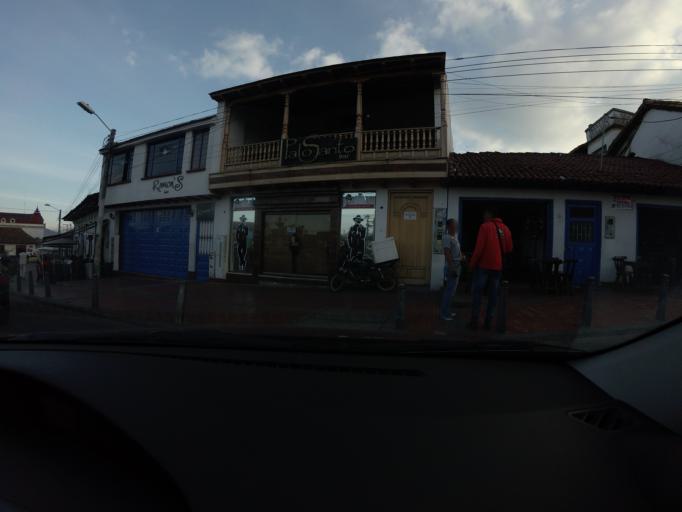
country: CO
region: Cundinamarca
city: Zipaquira
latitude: 5.0242
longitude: -74.0057
